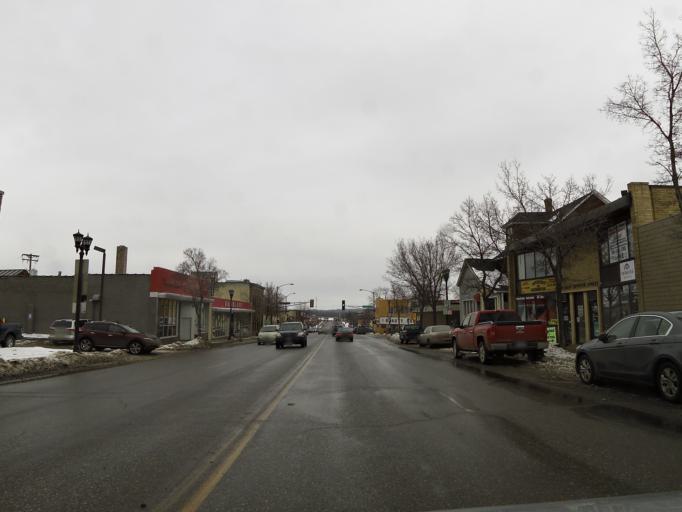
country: US
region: Minnesota
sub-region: Ramsey County
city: Saint Paul
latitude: 44.9613
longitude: -93.0670
